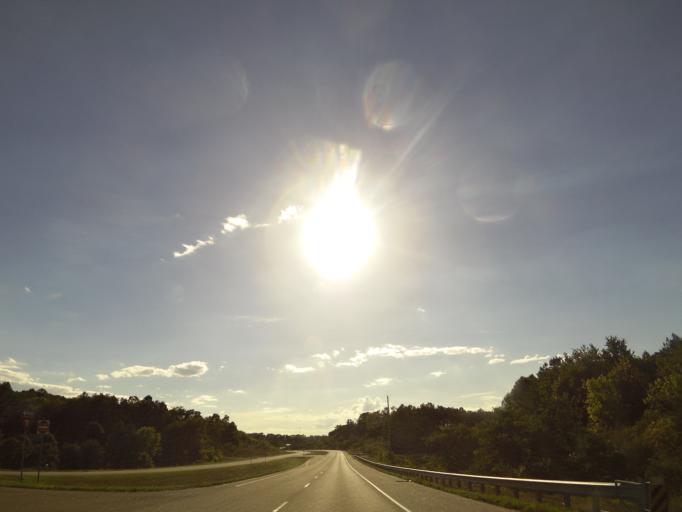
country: US
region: Tennessee
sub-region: Cocke County
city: Newport
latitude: 36.0056
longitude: -83.0800
